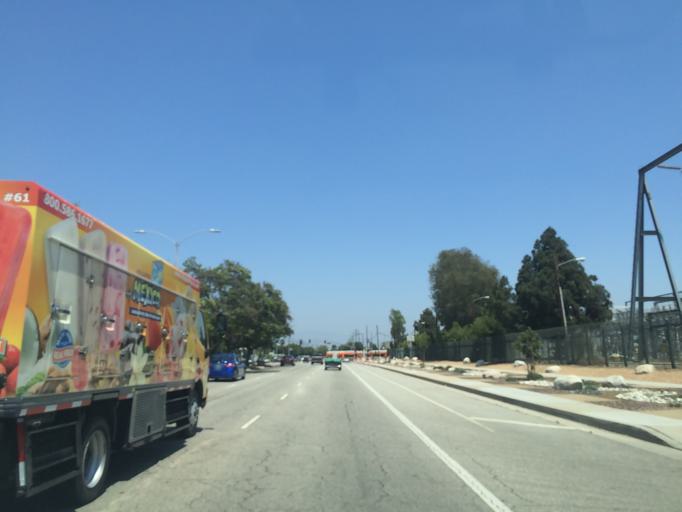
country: US
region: California
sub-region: Los Angeles County
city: Culver City
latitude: 34.0387
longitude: -118.3716
